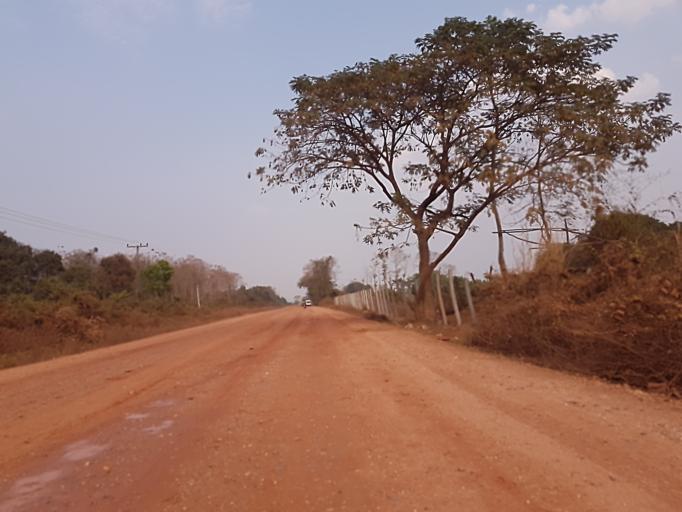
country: TH
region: Nong Khai
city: Nong Khai
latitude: 17.9779
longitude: 102.8679
